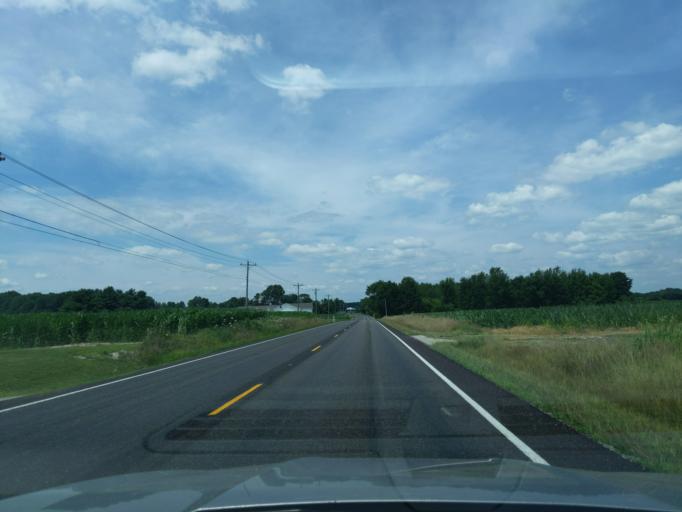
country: US
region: Indiana
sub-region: Ripley County
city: Osgood
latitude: 39.2391
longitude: -85.3443
